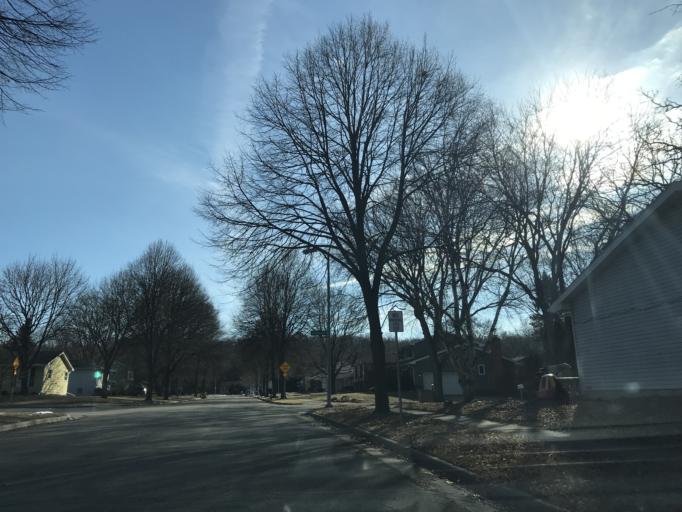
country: US
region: Wisconsin
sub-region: Dane County
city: Maple Bluff
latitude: 43.1403
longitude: -89.3087
